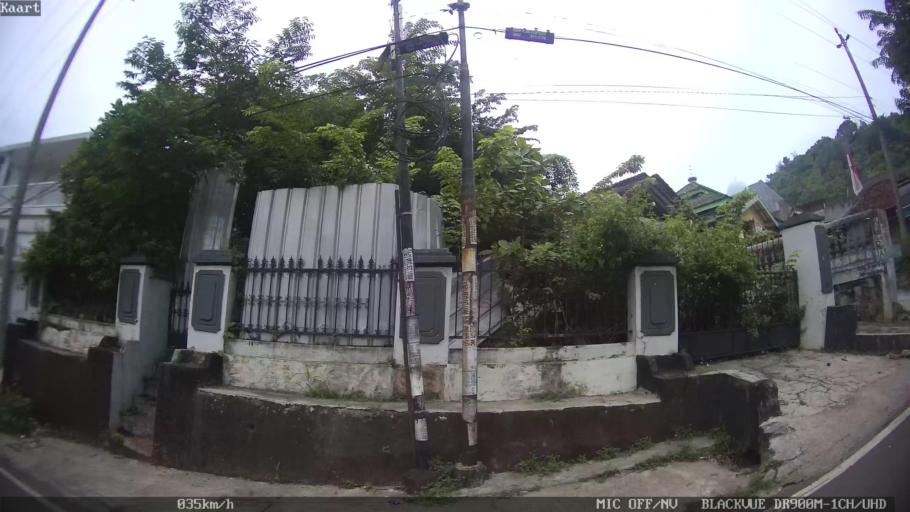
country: ID
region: Lampung
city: Bandarlampung
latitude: -5.4082
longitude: 105.2431
